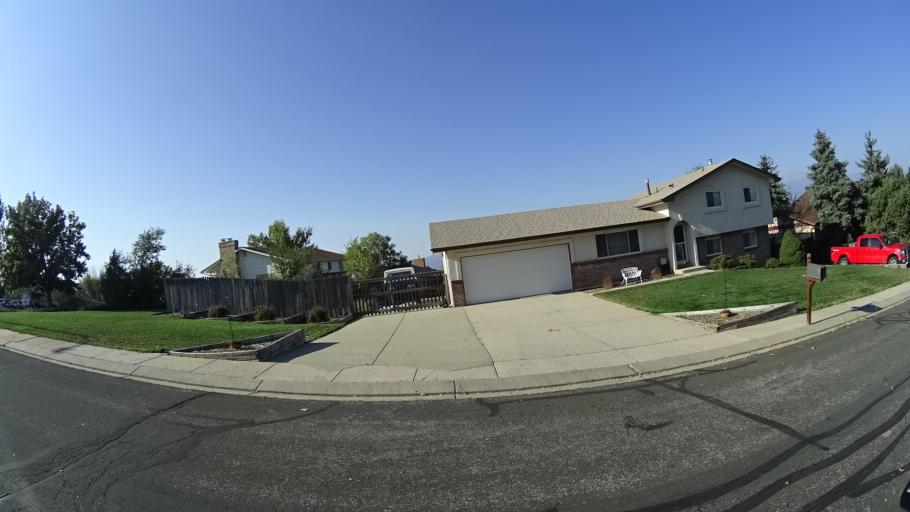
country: US
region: Colorado
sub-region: El Paso County
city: Cimarron Hills
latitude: 38.8905
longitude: -104.7300
